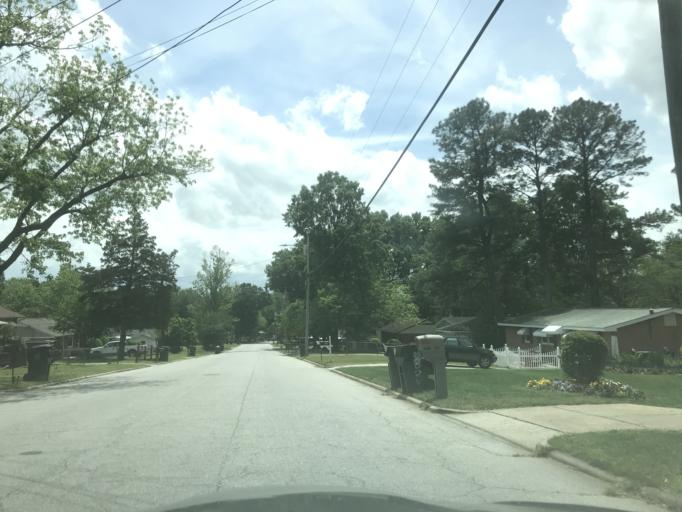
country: US
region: North Carolina
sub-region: Wake County
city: Raleigh
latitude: 35.7676
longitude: -78.5952
